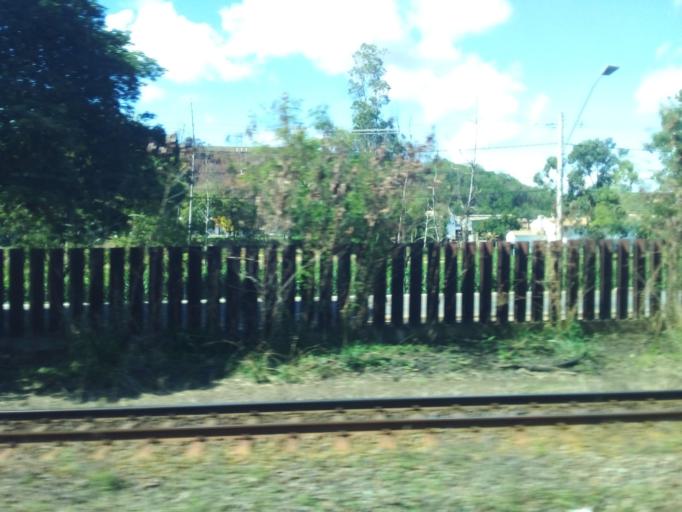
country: BR
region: Minas Gerais
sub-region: Governador Valadares
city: Governador Valadares
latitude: -18.8361
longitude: -41.8888
